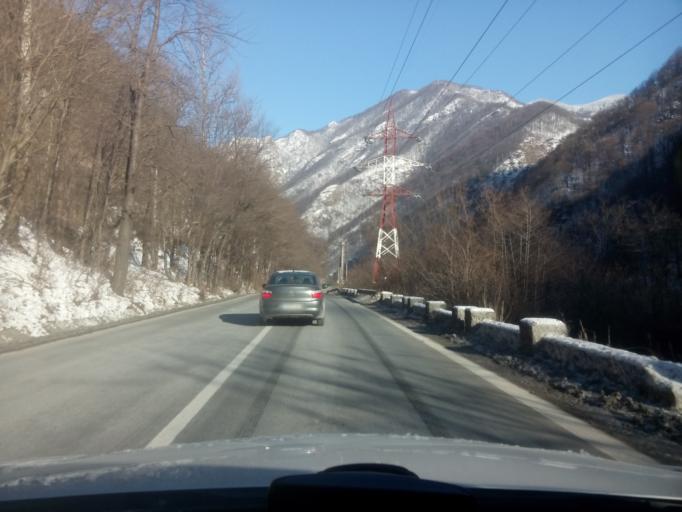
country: RO
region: Valcea
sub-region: Comuna Brezoi
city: Brezoi
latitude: 45.3141
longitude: 24.2764
